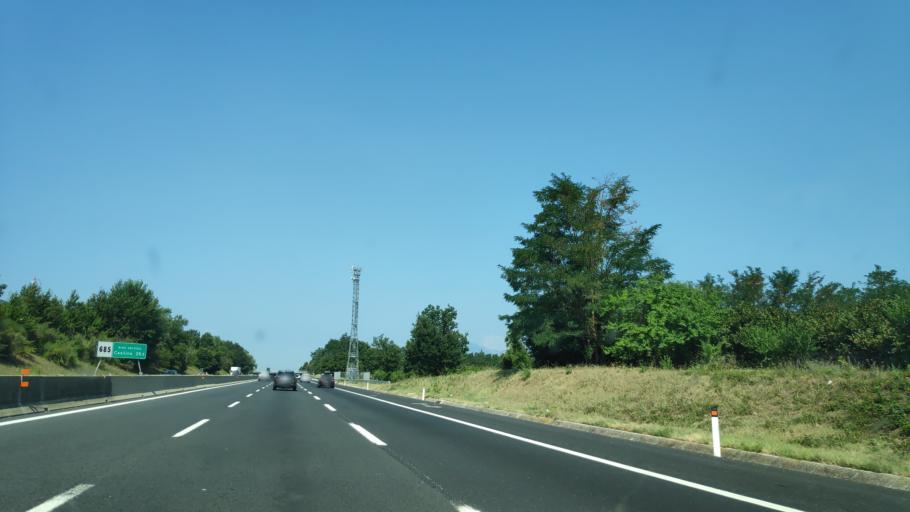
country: IT
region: Campania
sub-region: Provincia di Caserta
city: Mignano Monte Lungo
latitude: 41.4074
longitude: 13.9629
